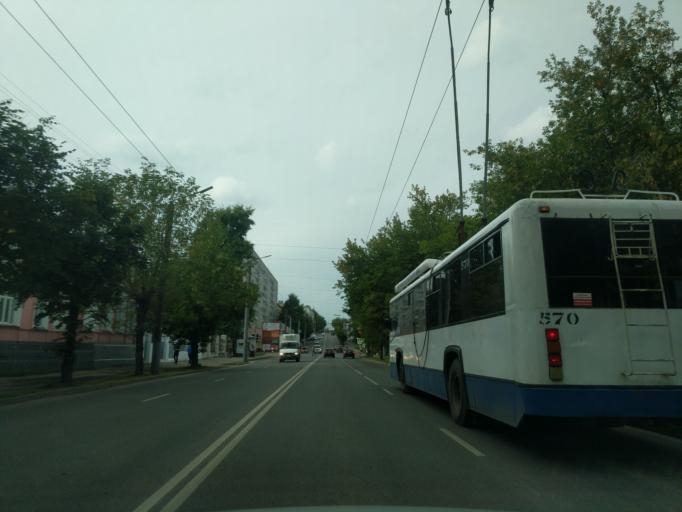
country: RU
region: Kirov
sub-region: Kirovo-Chepetskiy Rayon
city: Kirov
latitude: 58.5884
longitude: 49.6695
